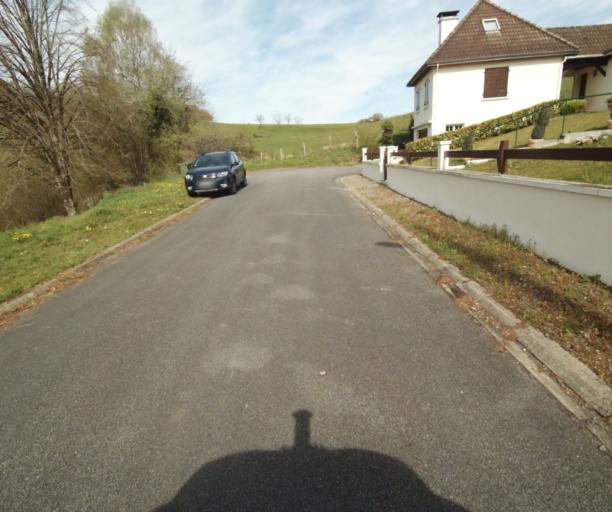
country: FR
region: Limousin
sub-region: Departement de la Correze
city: Laguenne
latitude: 45.2617
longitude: 1.8103
